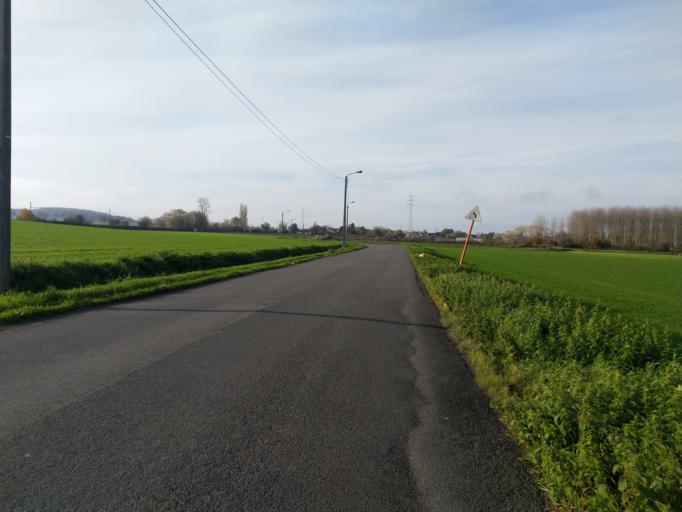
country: BE
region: Wallonia
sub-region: Province du Hainaut
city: Boussu
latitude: 50.4342
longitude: 3.7818
